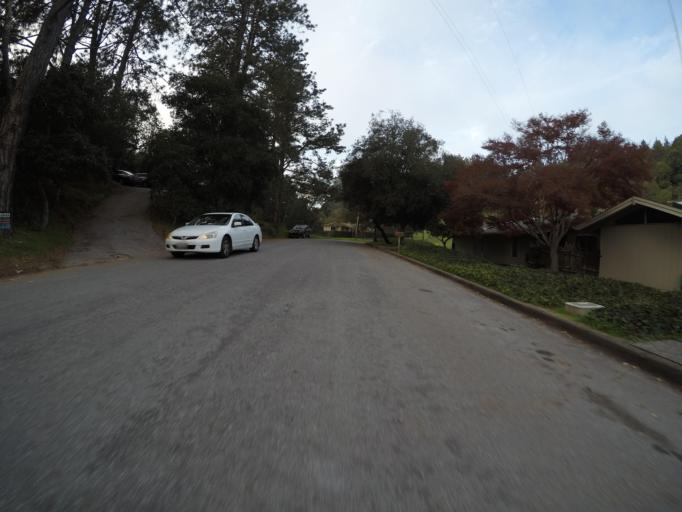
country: US
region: California
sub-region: Santa Cruz County
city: Pasatiempo
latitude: 37.0222
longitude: -122.0344
